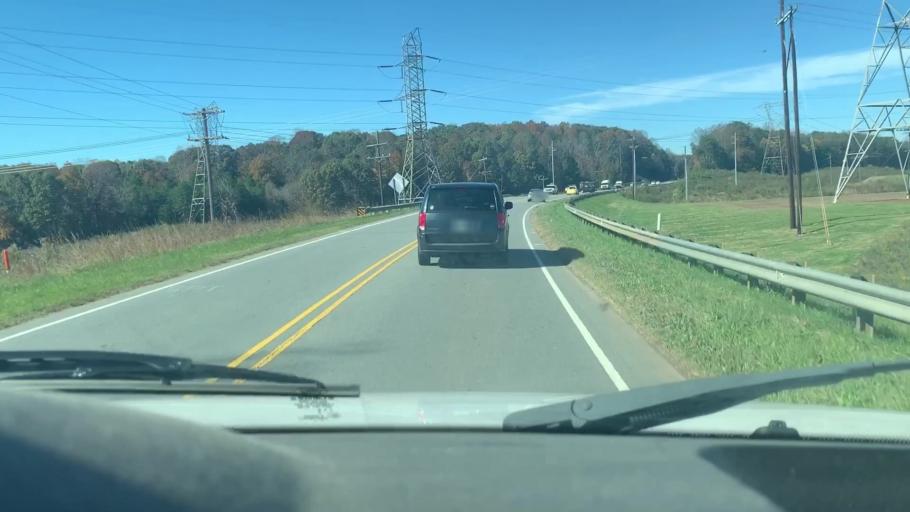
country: US
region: North Carolina
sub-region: Lincoln County
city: Lowesville
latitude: 35.4284
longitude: -80.9615
